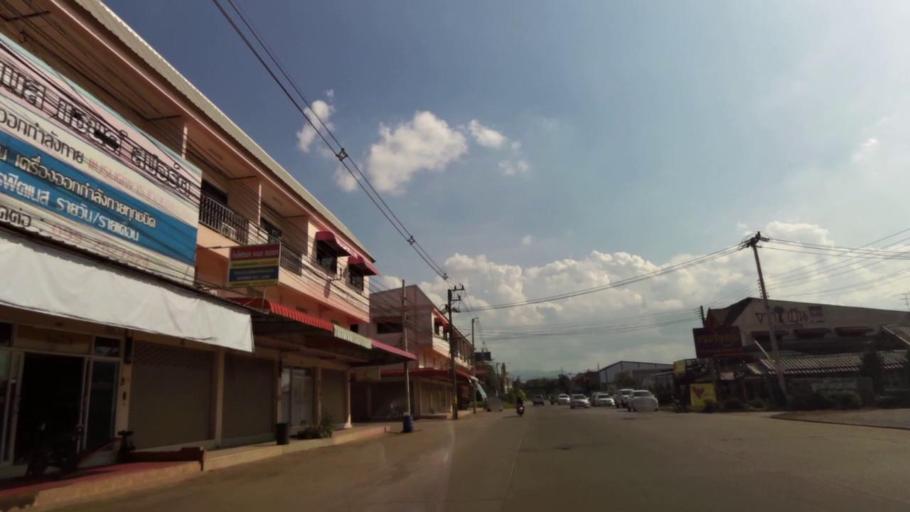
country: TH
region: Phrae
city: Phrae
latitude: 18.1208
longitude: 100.1543
